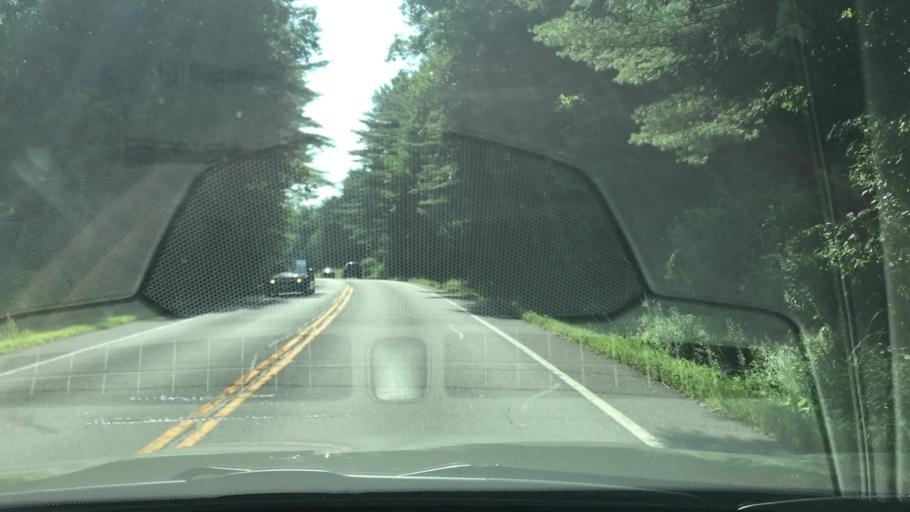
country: US
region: New York
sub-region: Warren County
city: Queensbury
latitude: 43.4080
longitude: -73.5715
